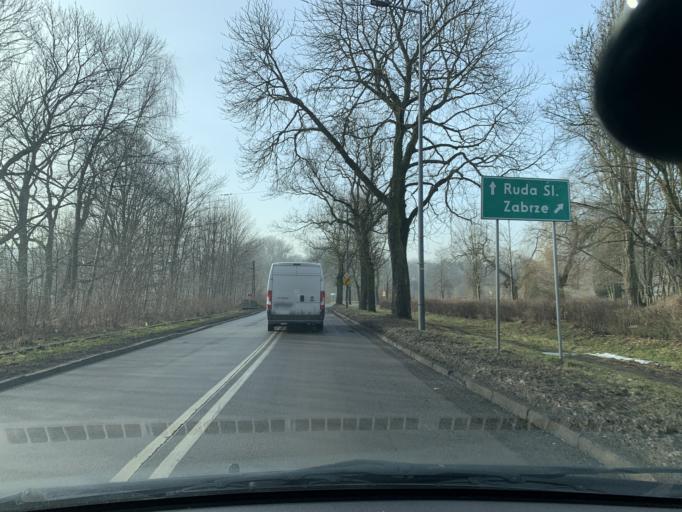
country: PL
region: Silesian Voivodeship
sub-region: Swietochlowice
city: Swietochlowice
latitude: 50.3300
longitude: 18.8635
